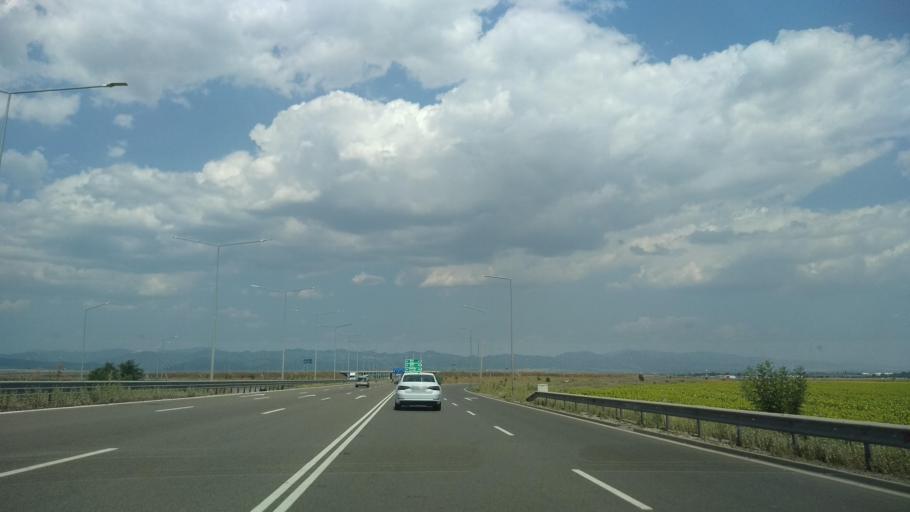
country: BG
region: Sofia-Capital
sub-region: Stolichna Obshtina
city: Sofia
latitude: 42.7487
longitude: 23.3118
